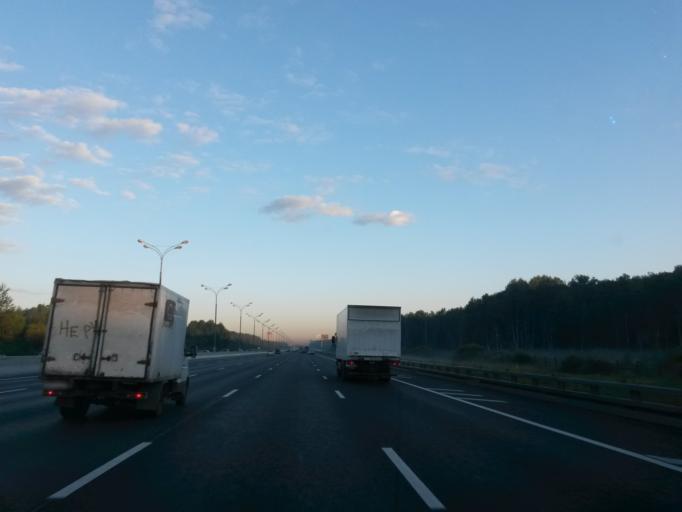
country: RU
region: Moskovskaya
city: Druzhba
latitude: 55.8642
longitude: 37.7620
